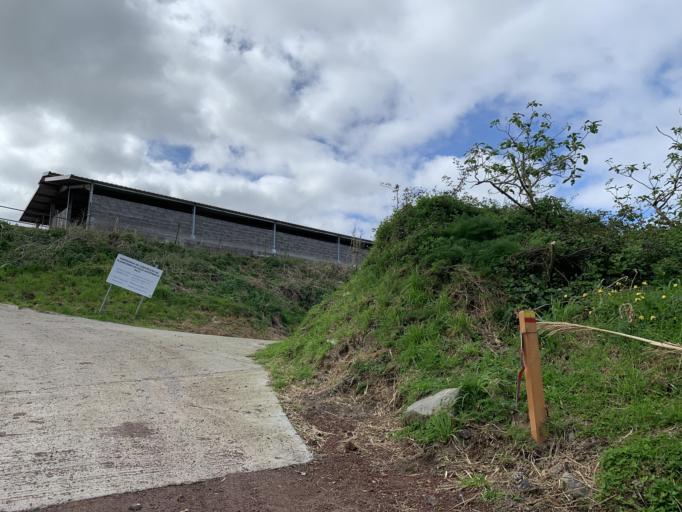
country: PT
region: Azores
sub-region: Ribeira Grande
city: Rabo de Peixe
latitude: 37.8043
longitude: -25.5037
